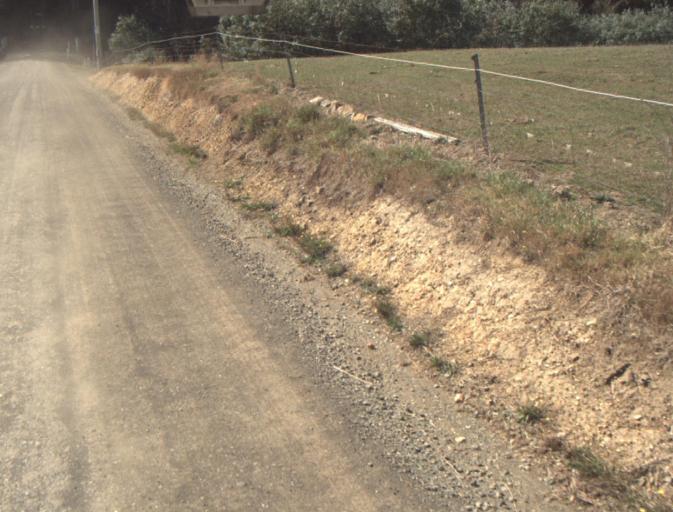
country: AU
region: Tasmania
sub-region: Launceston
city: Mayfield
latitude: -41.2241
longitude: 147.2370
